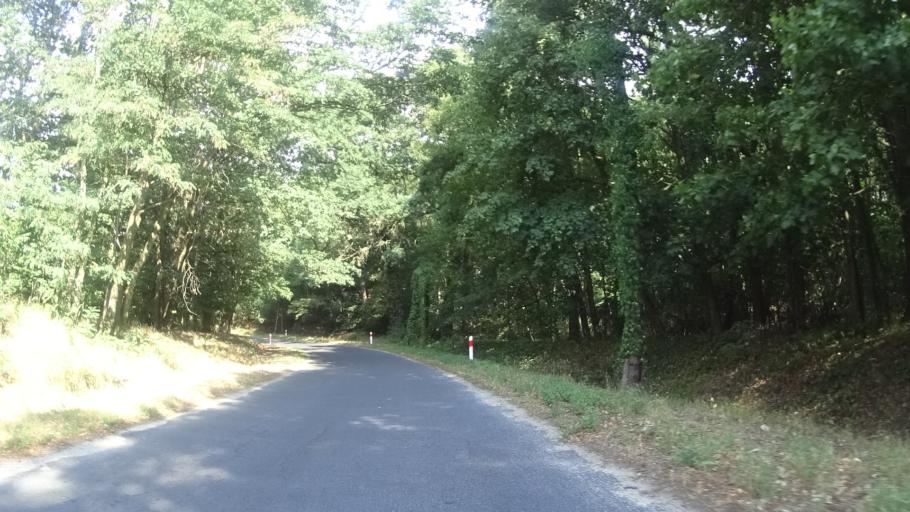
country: PL
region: Lubusz
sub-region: Powiat zarski
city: Przewoz
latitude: 51.4896
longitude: 14.8969
